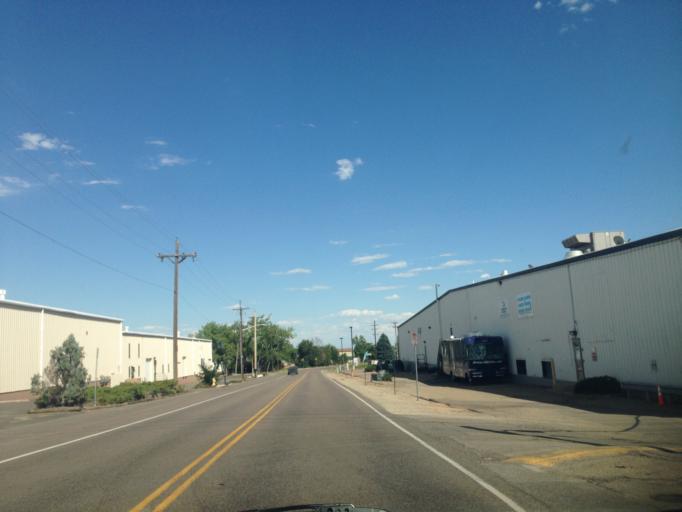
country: US
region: Colorado
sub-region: Broomfield County
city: Broomfield
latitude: 39.9214
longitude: -105.1001
